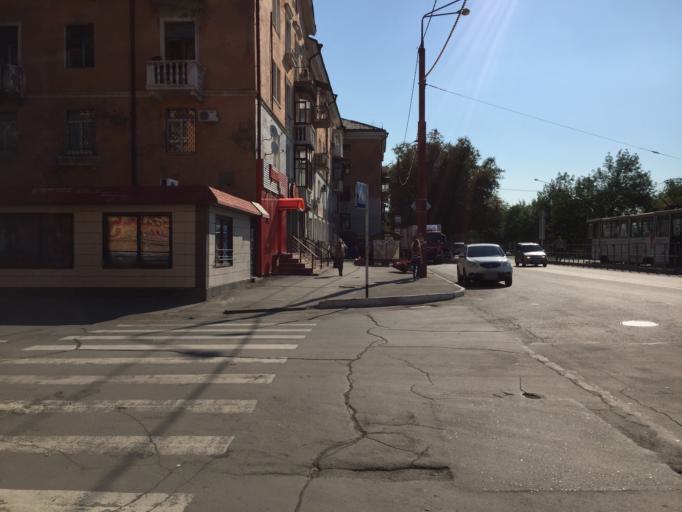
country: RU
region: Orenburg
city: Novotroitsk
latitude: 51.1958
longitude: 58.3246
